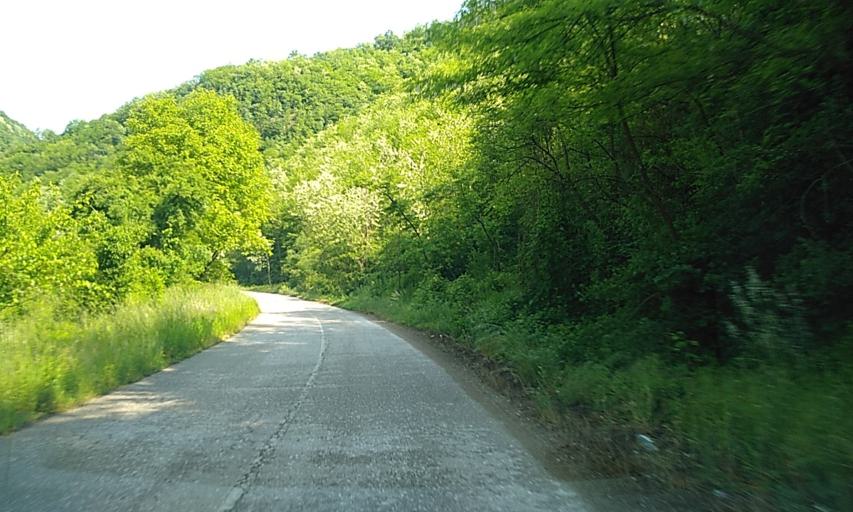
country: RS
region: Central Serbia
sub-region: Pcinjski Okrug
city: Vladicin Han
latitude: 42.7547
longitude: 22.0680
